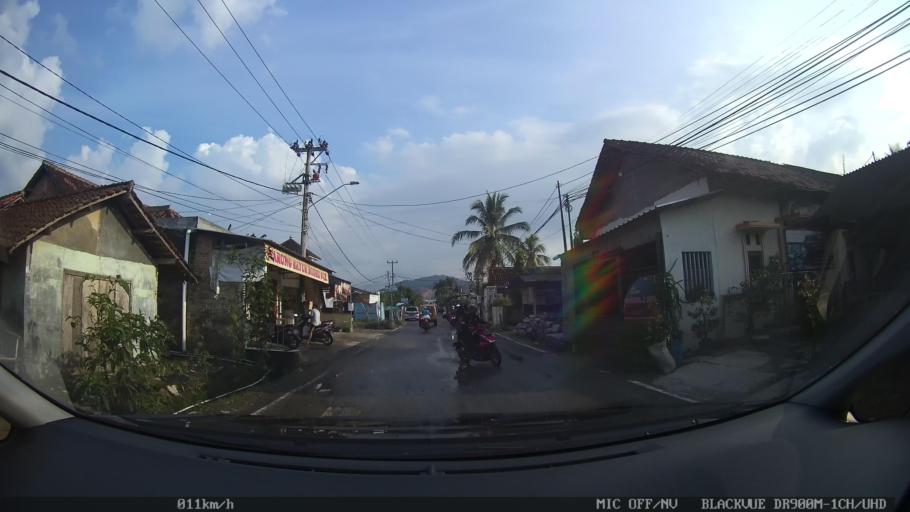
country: ID
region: Lampung
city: Kedaton
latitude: -5.3911
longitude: 105.3156
